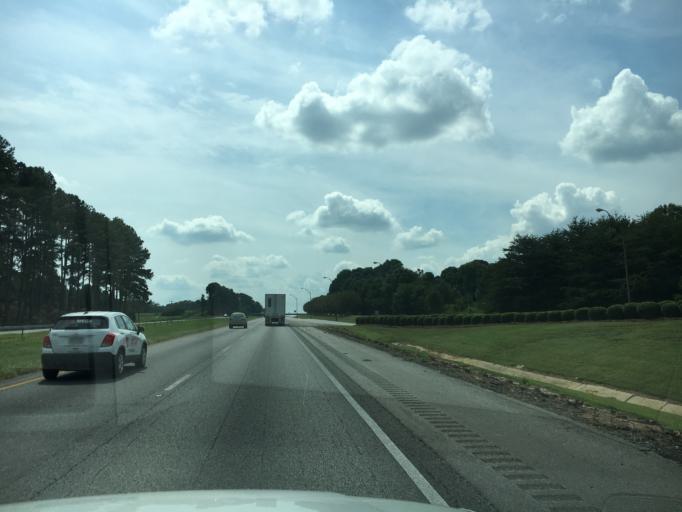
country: US
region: Georgia
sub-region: Franklin County
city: Gumlog
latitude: 34.4699
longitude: -83.0704
